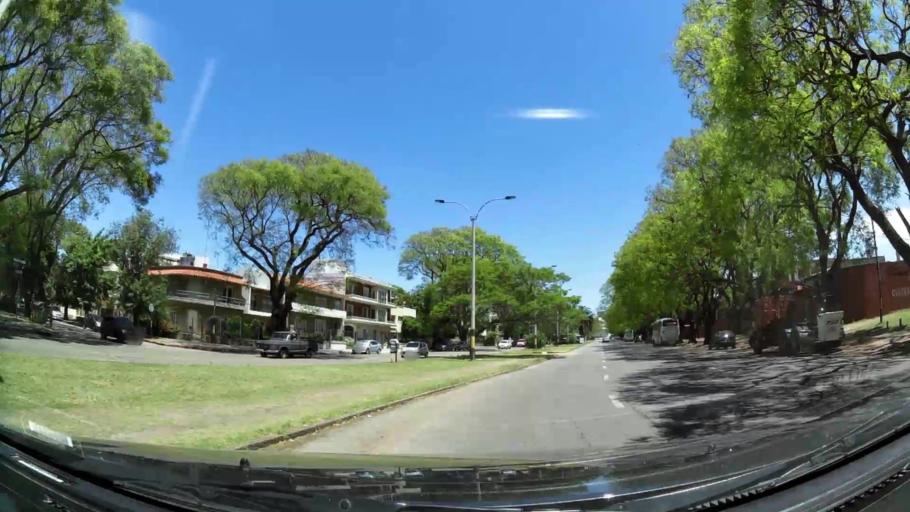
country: UY
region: Montevideo
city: Montevideo
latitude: -34.8985
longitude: -56.1524
